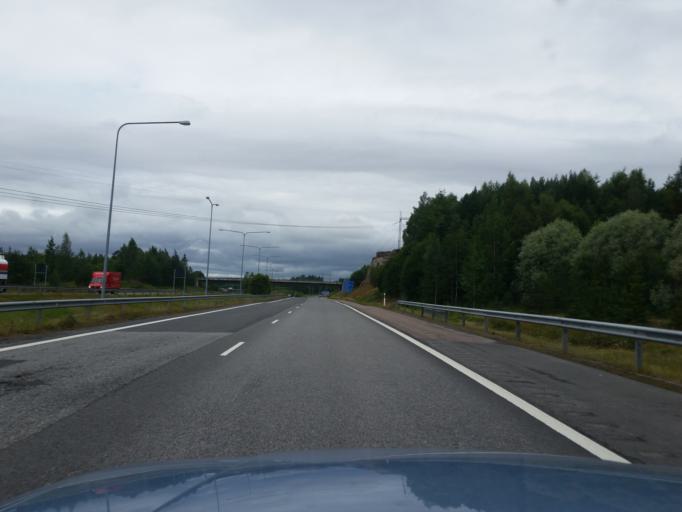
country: FI
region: Varsinais-Suomi
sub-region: Turku
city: Kaarina
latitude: 60.4243
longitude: 22.3993
